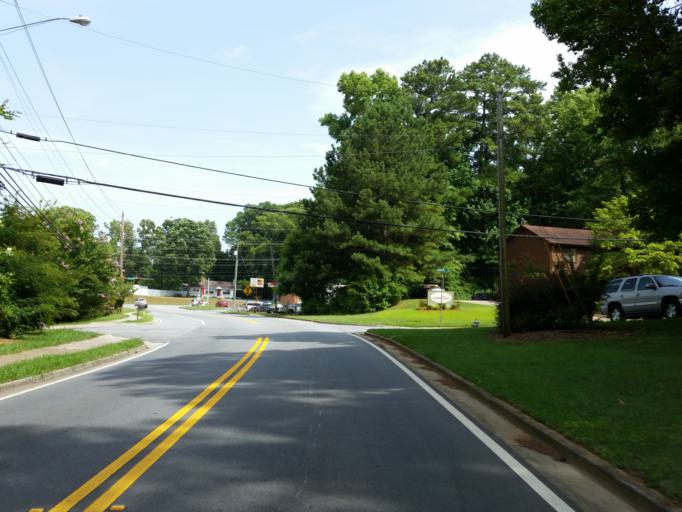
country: US
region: Georgia
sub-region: Cherokee County
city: Woodstock
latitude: 34.0501
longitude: -84.5290
